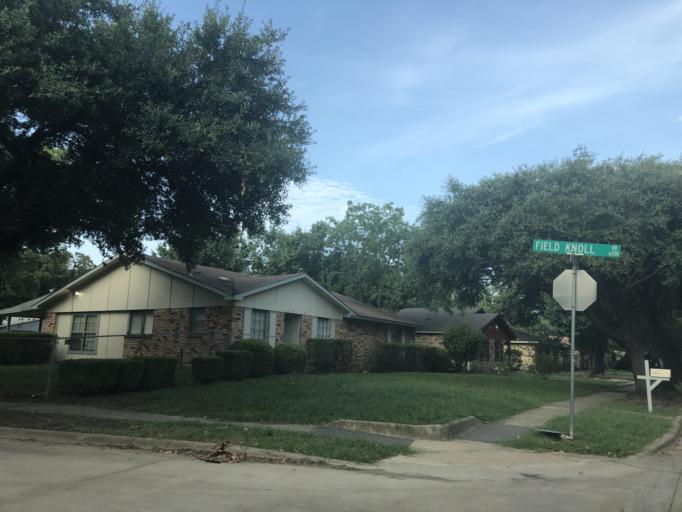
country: US
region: Texas
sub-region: Dallas County
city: Sunnyvale
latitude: 32.8395
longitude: -96.5864
